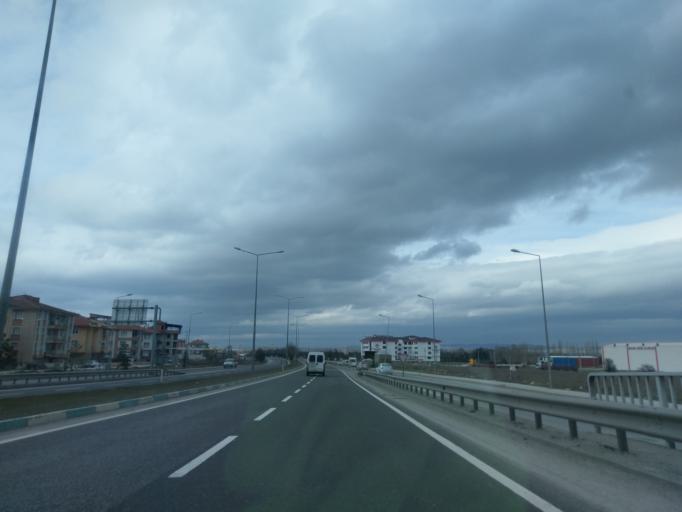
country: TR
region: Kuetahya
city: Kutahya
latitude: 39.4071
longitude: 30.0265
